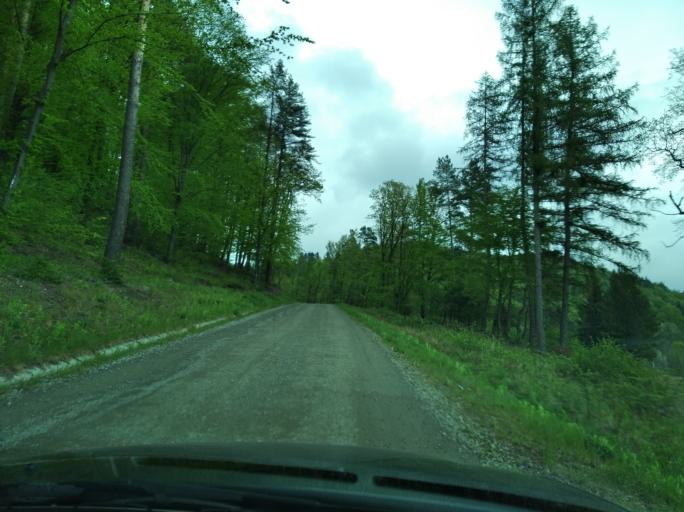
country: PL
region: Subcarpathian Voivodeship
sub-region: Powiat sanocki
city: Sanok
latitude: 49.5648
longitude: 22.2331
